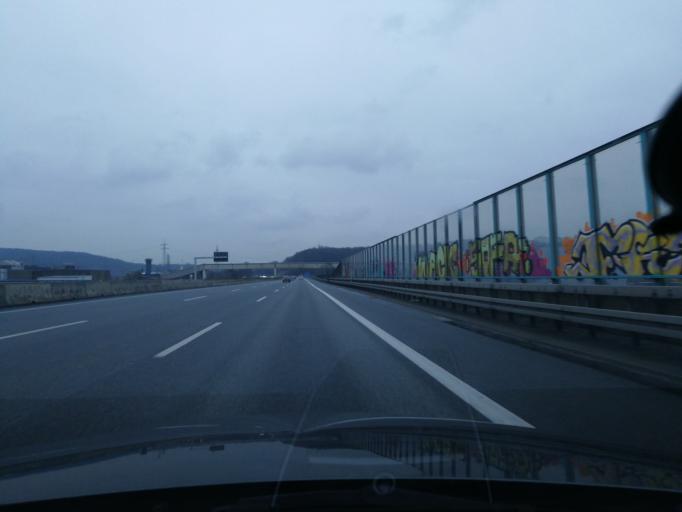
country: DE
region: North Rhine-Westphalia
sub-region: Regierungsbezirk Arnsberg
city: Hagen
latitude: 51.4076
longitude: 7.4850
